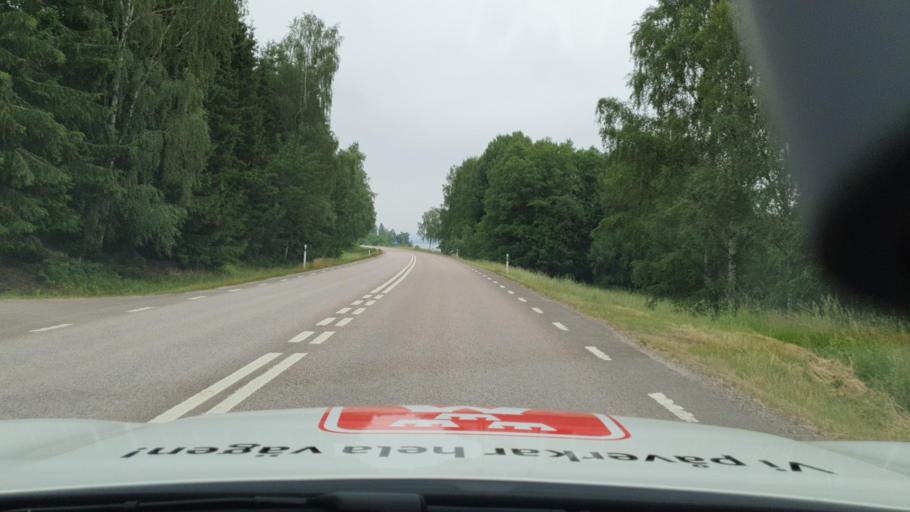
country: SE
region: Vaermland
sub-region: Sunne Kommun
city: Sunne
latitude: 59.8751
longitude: 13.1417
